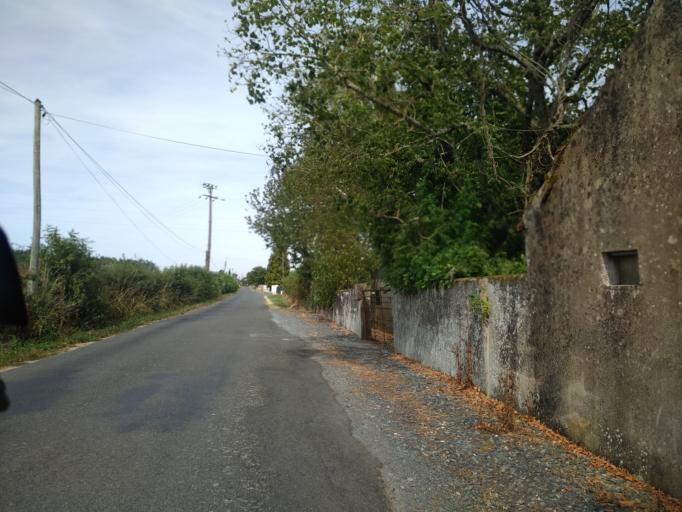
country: FR
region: Bourgogne
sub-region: Departement de Saone-et-Loire
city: Bourbon-Lancy
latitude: 46.6147
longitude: 3.7513
